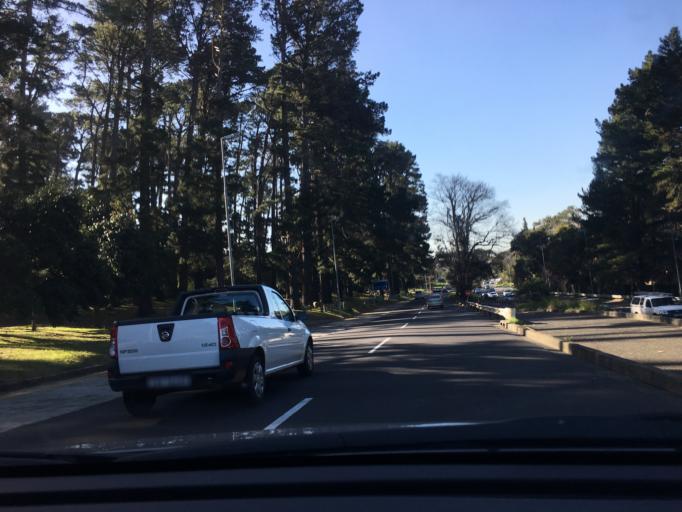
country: ZA
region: Western Cape
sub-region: City of Cape Town
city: Newlands
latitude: -33.9676
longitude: 18.4554
